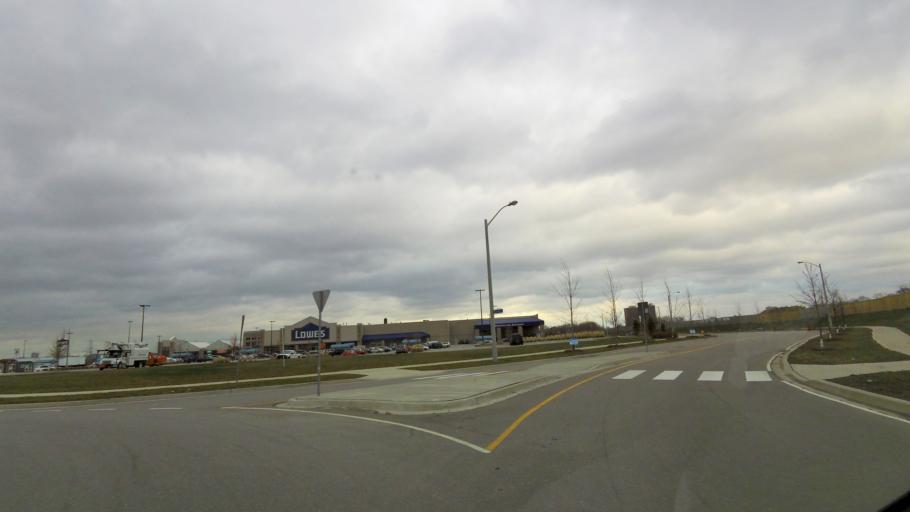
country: CA
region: Ontario
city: Etobicoke
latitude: 43.7078
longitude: -79.5498
